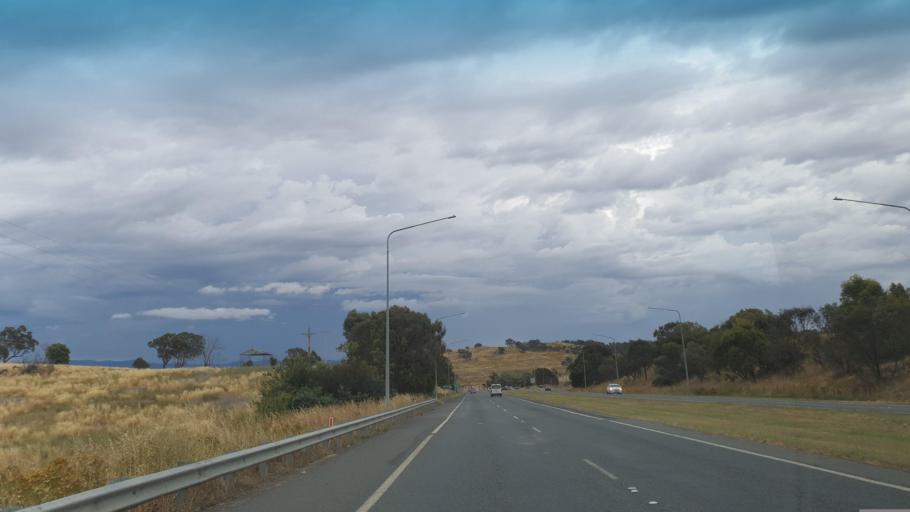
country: AU
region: Australian Capital Territory
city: Macquarie
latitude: -35.2716
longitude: 149.0570
